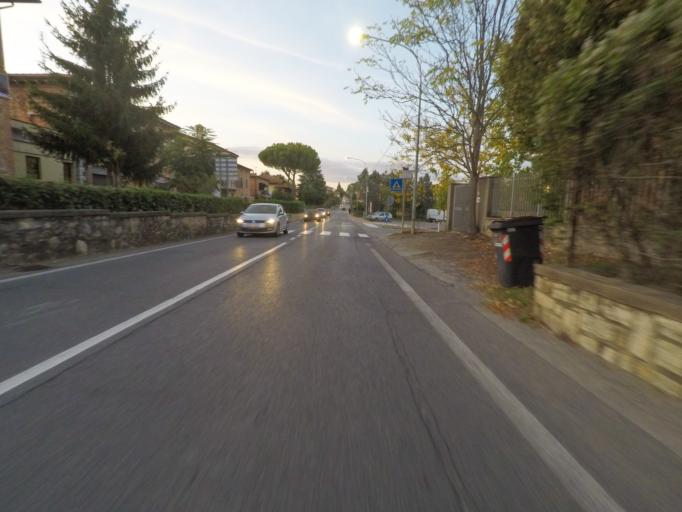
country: IT
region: Tuscany
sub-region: Provincia di Siena
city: Torrita di Siena
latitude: 43.1699
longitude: 11.7745
